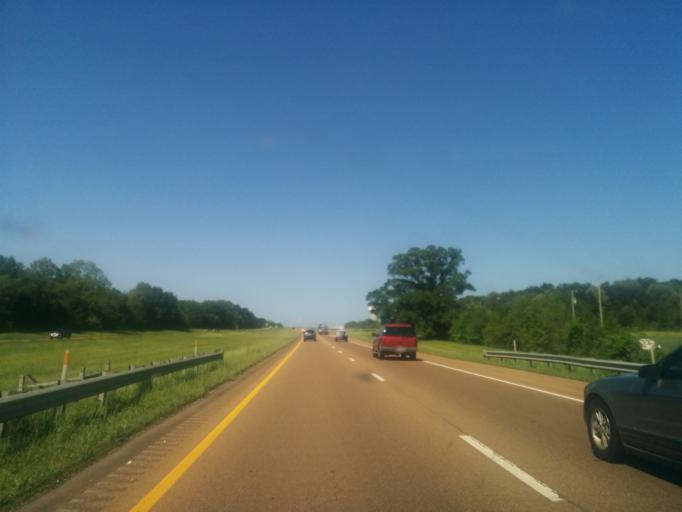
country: US
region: Mississippi
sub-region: Madison County
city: Canton
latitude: 32.5542
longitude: -90.0857
